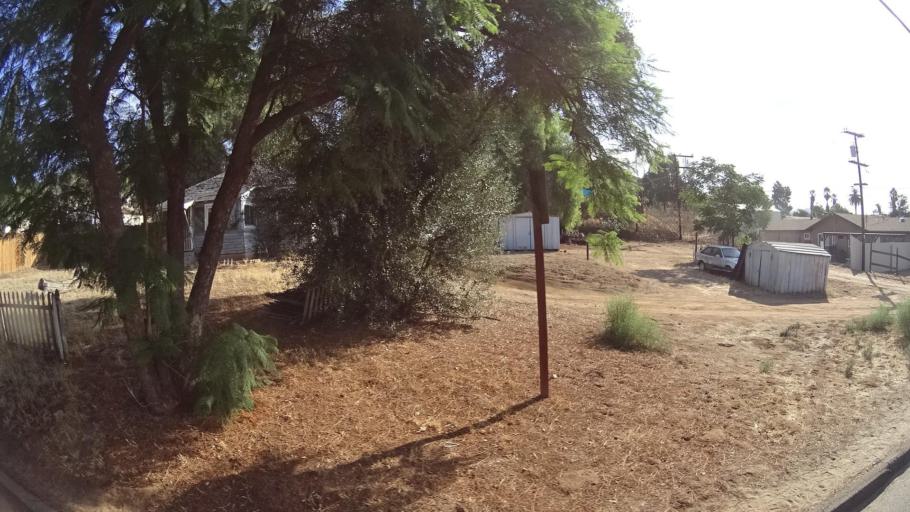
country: US
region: California
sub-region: San Diego County
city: Lakeside
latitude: 32.8680
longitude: -116.9320
